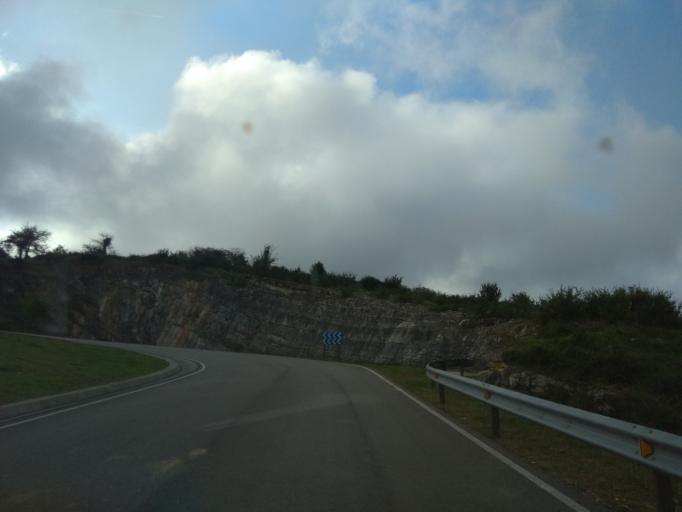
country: ES
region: Cantabria
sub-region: Provincia de Cantabria
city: San Vicente de la Barquera
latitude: 43.3087
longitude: -4.4017
